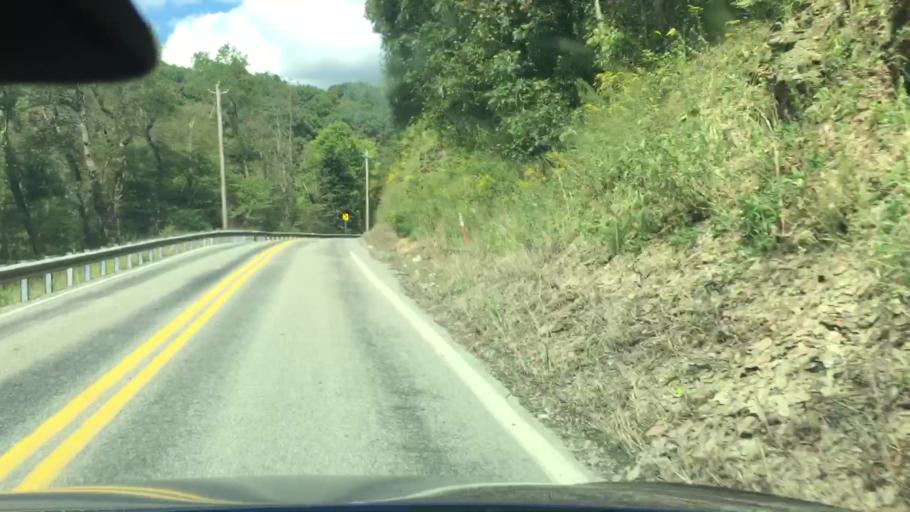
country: US
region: Pennsylvania
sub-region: Allegheny County
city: Curtisville
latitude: 40.6432
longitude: -79.8398
